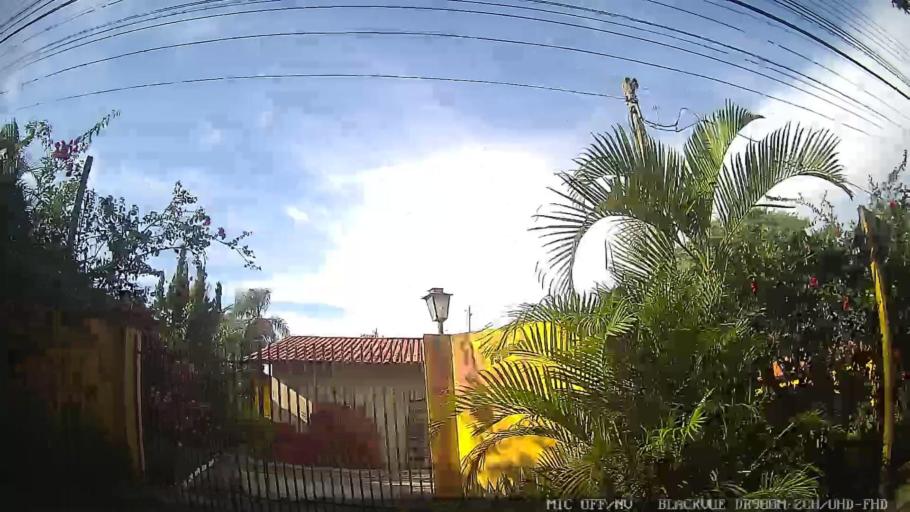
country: BR
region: Sao Paulo
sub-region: Tiete
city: Tiete
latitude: -23.0847
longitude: -47.6831
